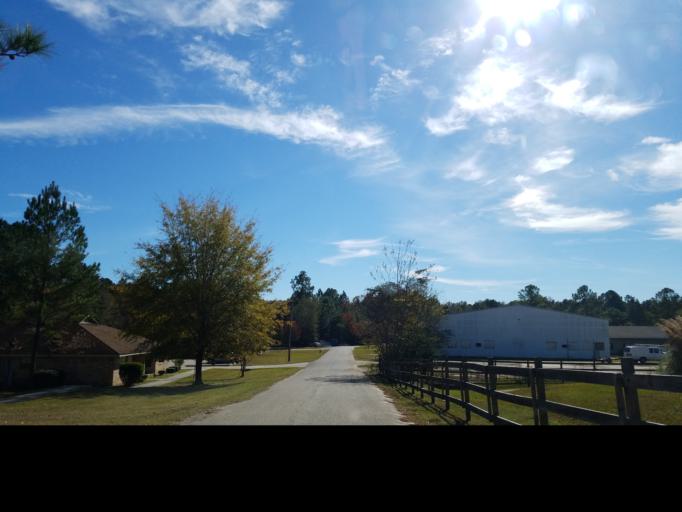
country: US
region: Mississippi
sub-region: Forrest County
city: Hattiesburg
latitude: 31.2760
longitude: -89.2823
